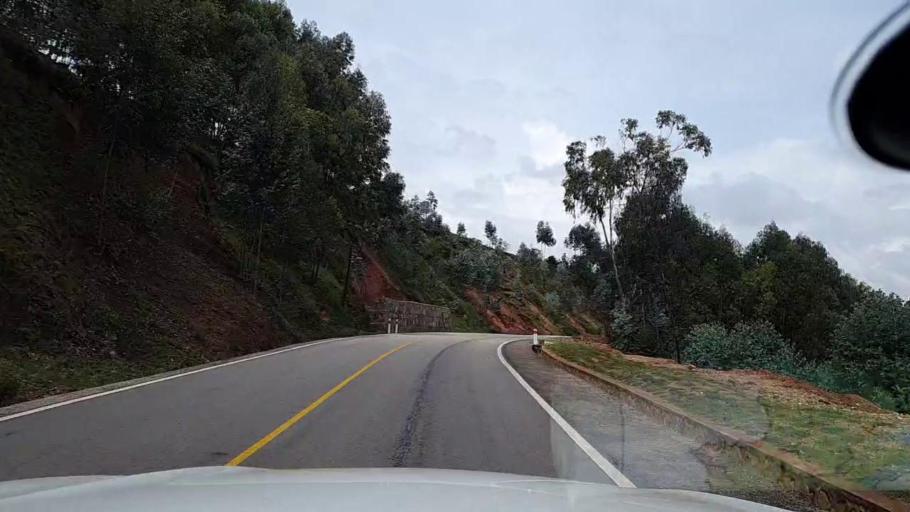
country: RW
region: Southern Province
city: Nzega
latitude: -2.5053
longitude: 29.5031
